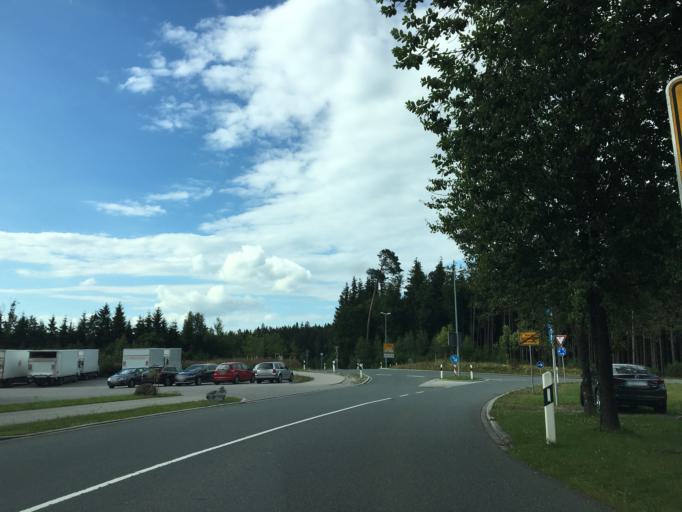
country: DE
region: Bavaria
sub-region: Upper Bavaria
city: Holzkirchen
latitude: 47.8809
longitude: 11.7171
